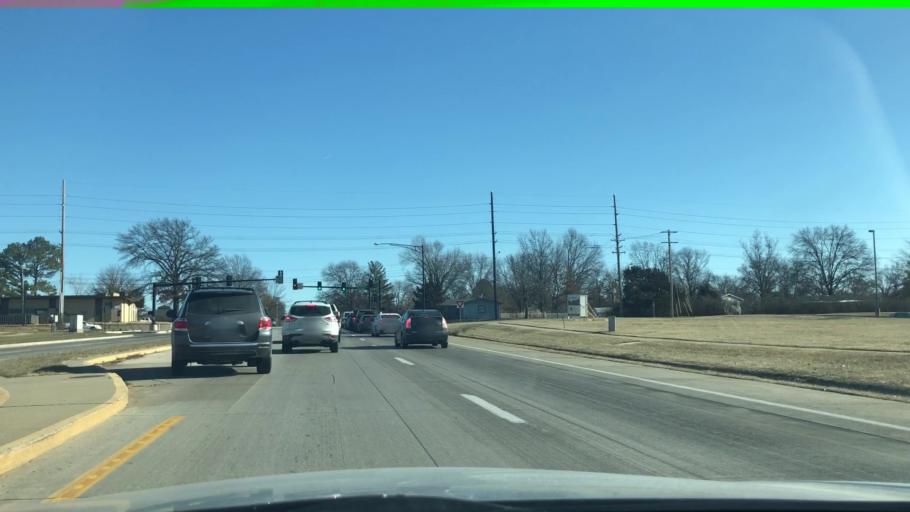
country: US
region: Missouri
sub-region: Boone County
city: Columbia
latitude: 38.9547
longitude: -92.3821
